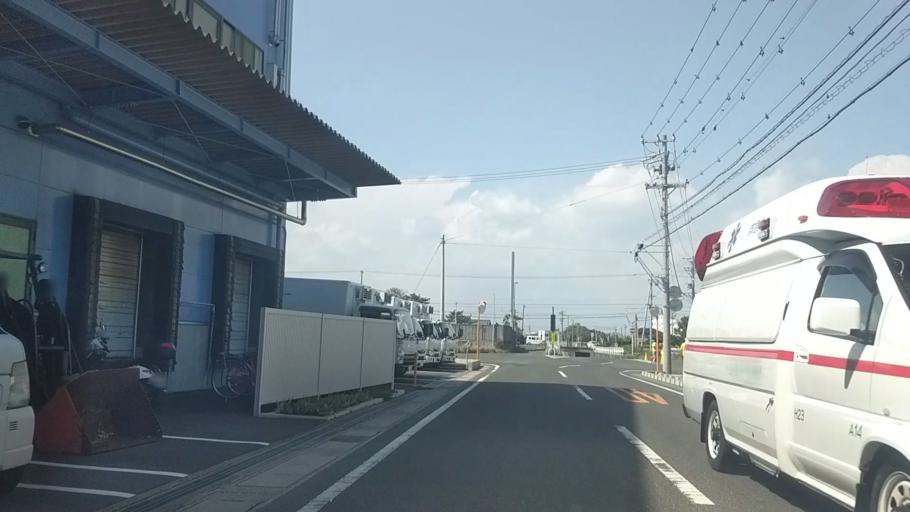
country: JP
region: Shizuoka
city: Hamamatsu
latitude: 34.6688
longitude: 137.7225
